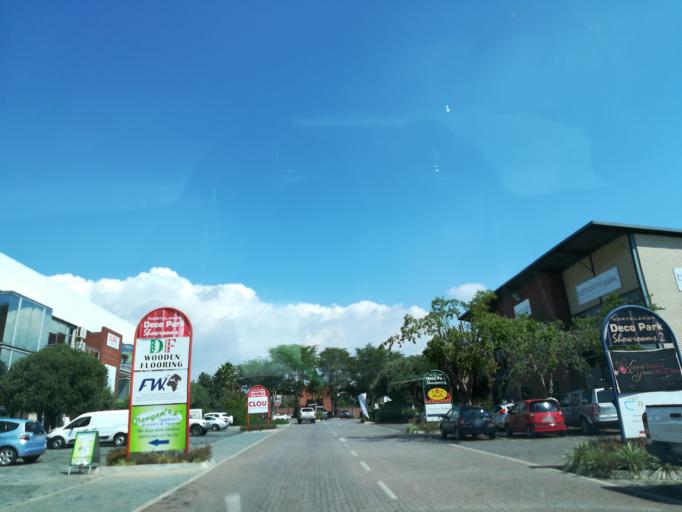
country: ZA
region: Gauteng
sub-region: City of Johannesburg Metropolitan Municipality
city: Diepsloot
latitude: -26.0372
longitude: 27.9576
